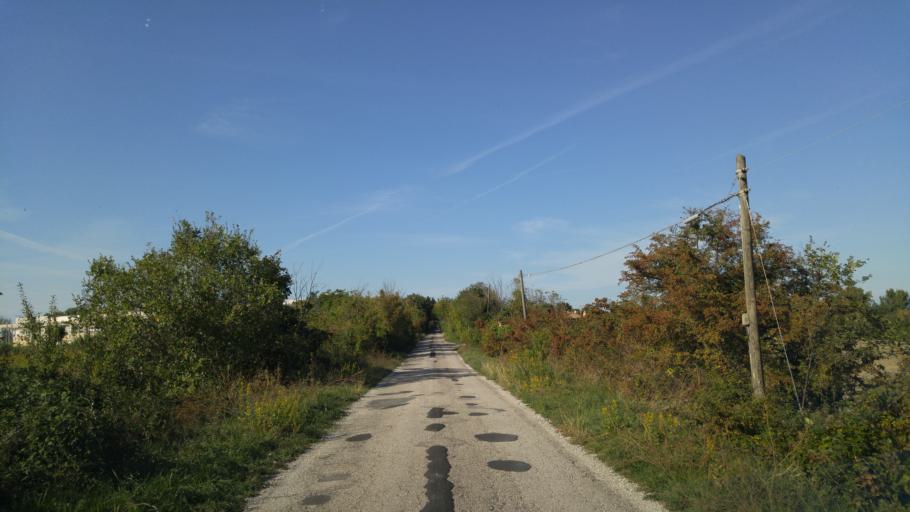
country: IT
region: The Marches
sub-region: Provincia di Pesaro e Urbino
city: Bellocchi
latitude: 43.7958
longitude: 13.0220
